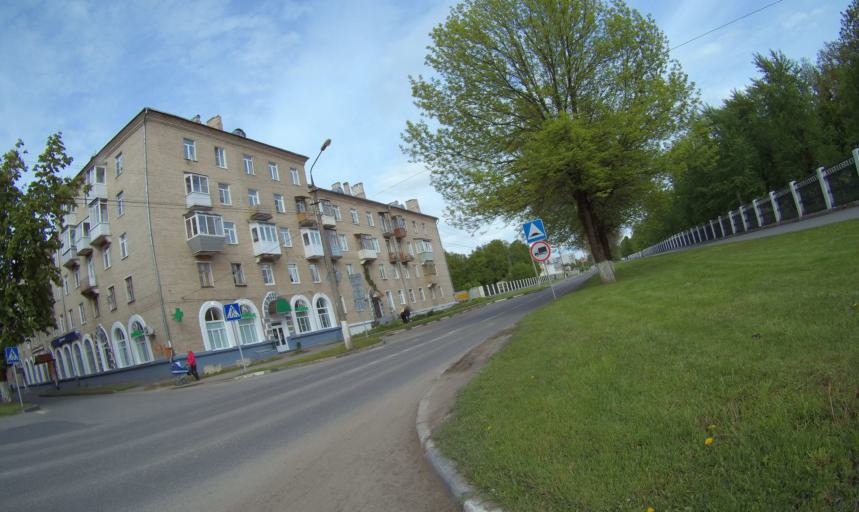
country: RU
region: Moskovskaya
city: Kolomna
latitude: 55.0880
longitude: 38.7792
